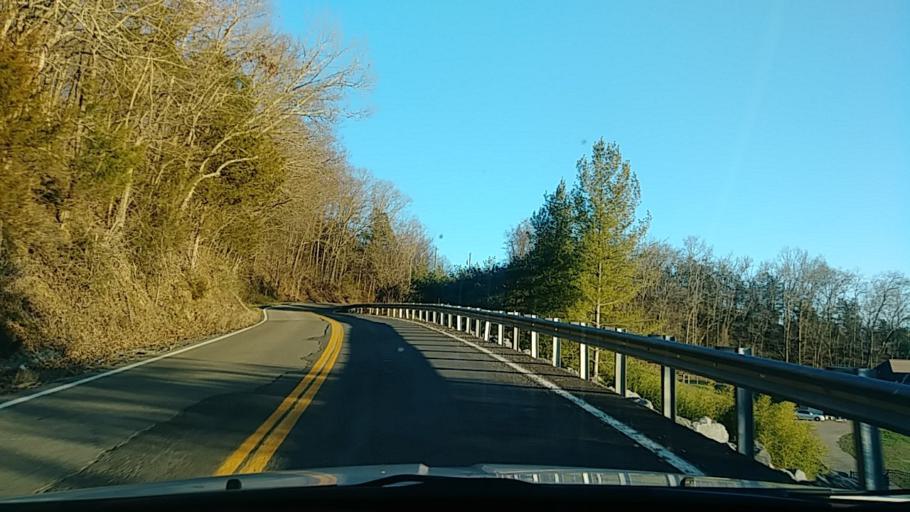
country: US
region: Tennessee
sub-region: Jefferson County
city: White Pine
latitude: 36.1250
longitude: -83.1228
